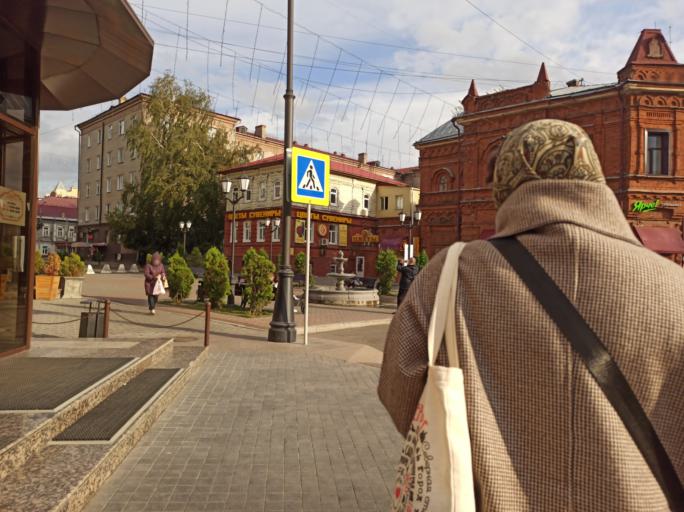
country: RU
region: Tomsk
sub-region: Tomskiy Rayon
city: Tomsk
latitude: 56.4793
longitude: 84.9499
